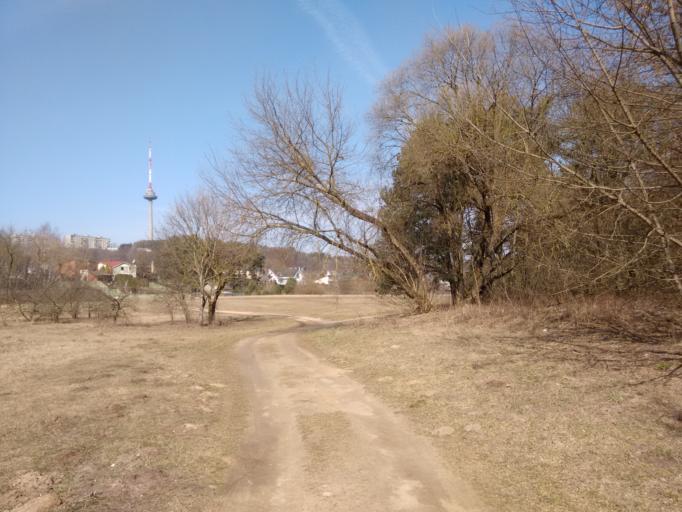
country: LT
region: Vilnius County
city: Vilkpede
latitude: 54.6781
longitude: 25.2304
